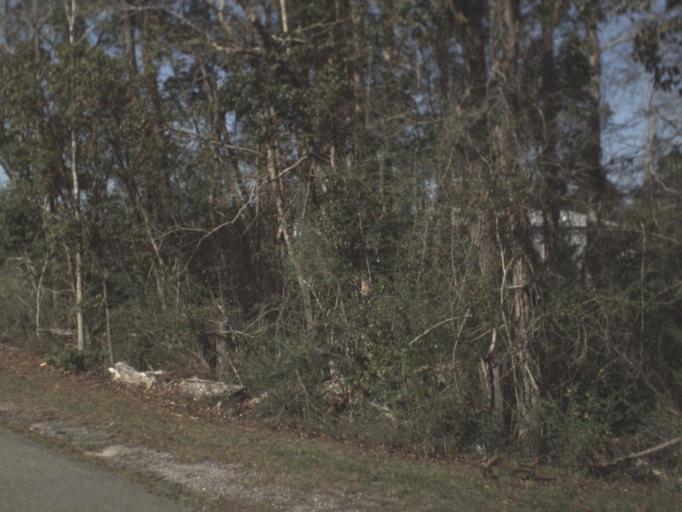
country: US
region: Florida
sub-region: Gulf County
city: Wewahitchka
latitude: 30.1347
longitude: -85.2082
